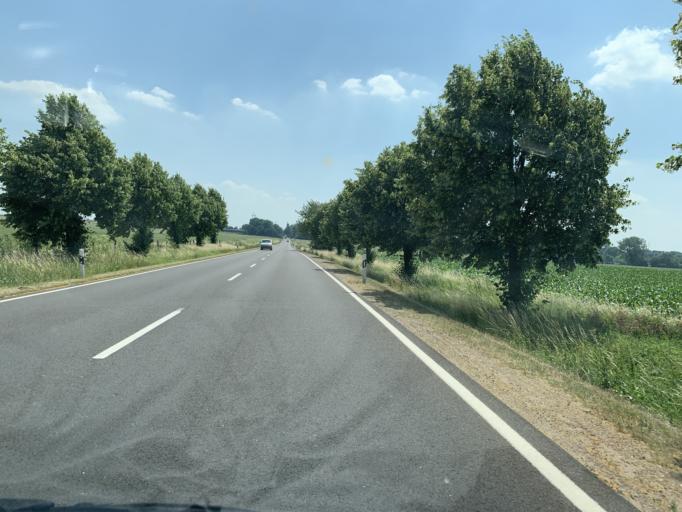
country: DE
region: Saxony-Anhalt
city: Erxleben
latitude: 52.1898
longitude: 11.2651
